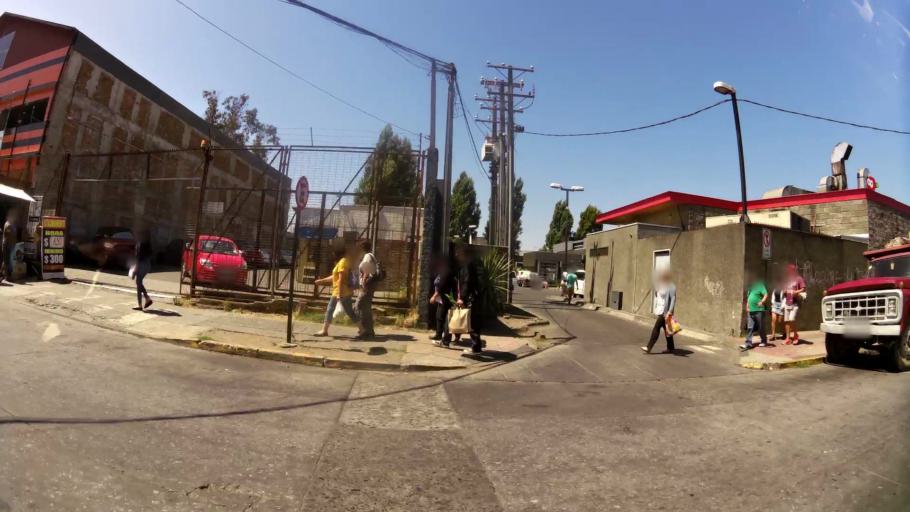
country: CL
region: Biobio
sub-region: Provincia de Concepcion
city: Concepcion
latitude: -36.8223
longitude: -73.0509
